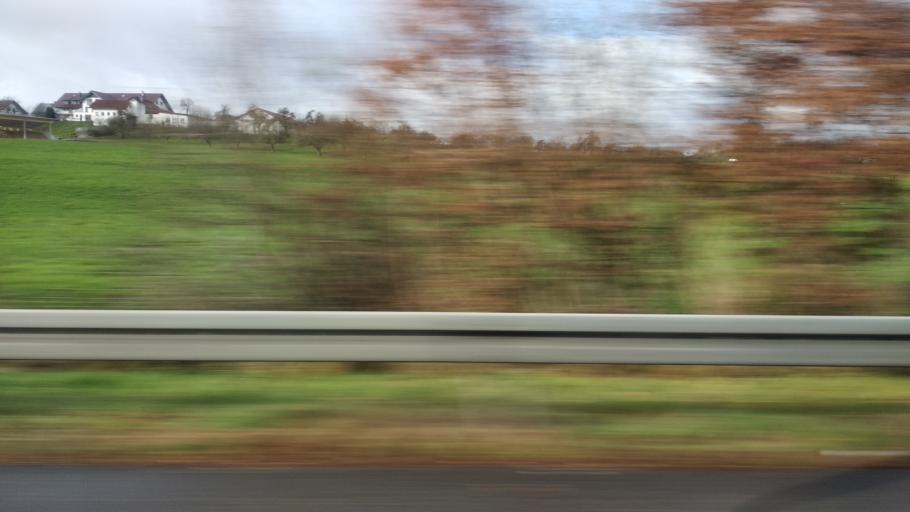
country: DE
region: Bavaria
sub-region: Swabia
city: Weissensberg
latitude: 47.6259
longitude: 9.7397
